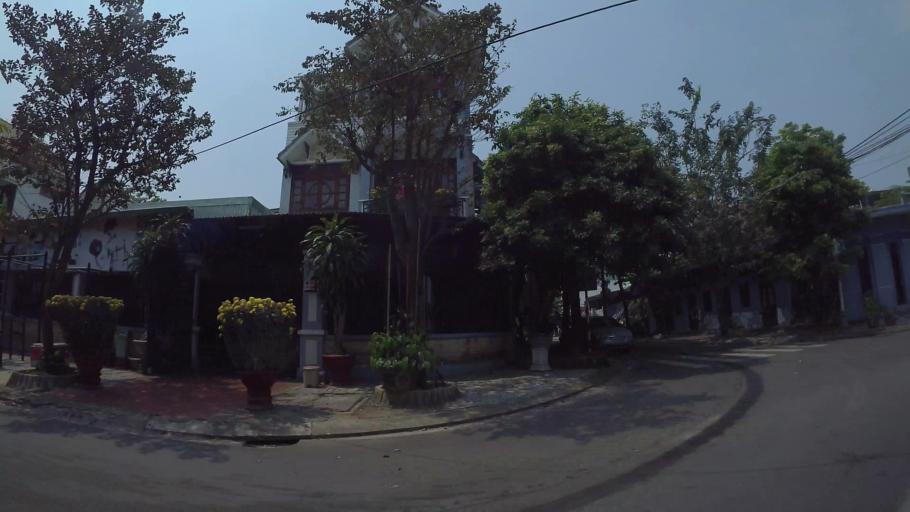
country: VN
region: Da Nang
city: Cam Le
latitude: 16.0059
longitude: 108.2157
